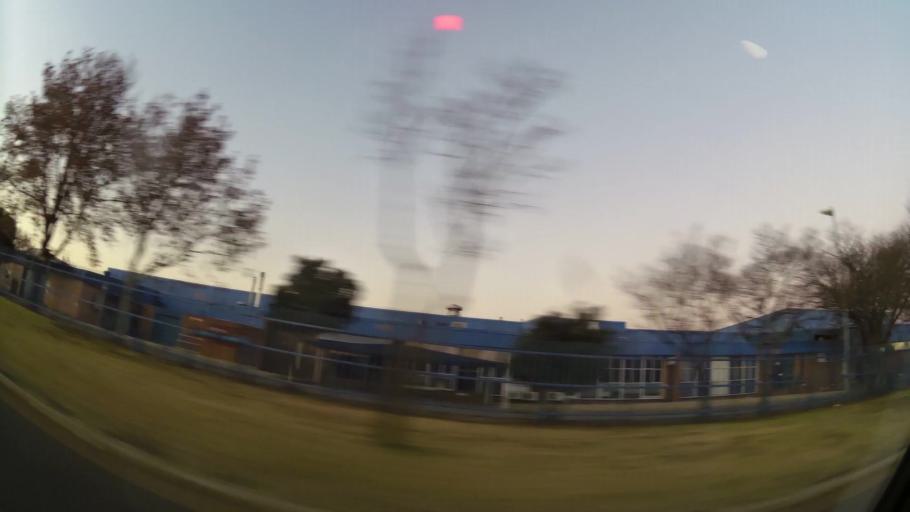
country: ZA
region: Gauteng
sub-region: Ekurhuleni Metropolitan Municipality
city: Germiston
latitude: -26.2689
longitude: 28.1729
